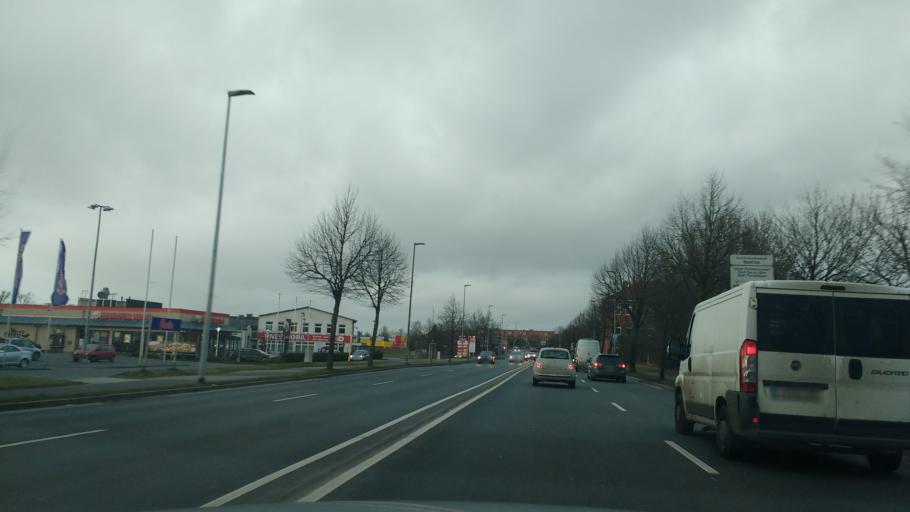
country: DE
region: Schleswig-Holstein
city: Itzehoe
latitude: 53.9145
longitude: 9.5159
